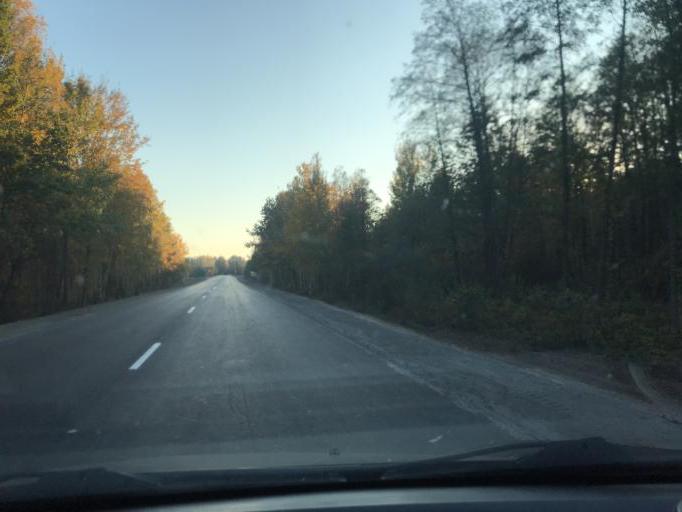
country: BY
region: Gomel
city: Brahin
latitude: 51.8636
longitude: 30.3727
